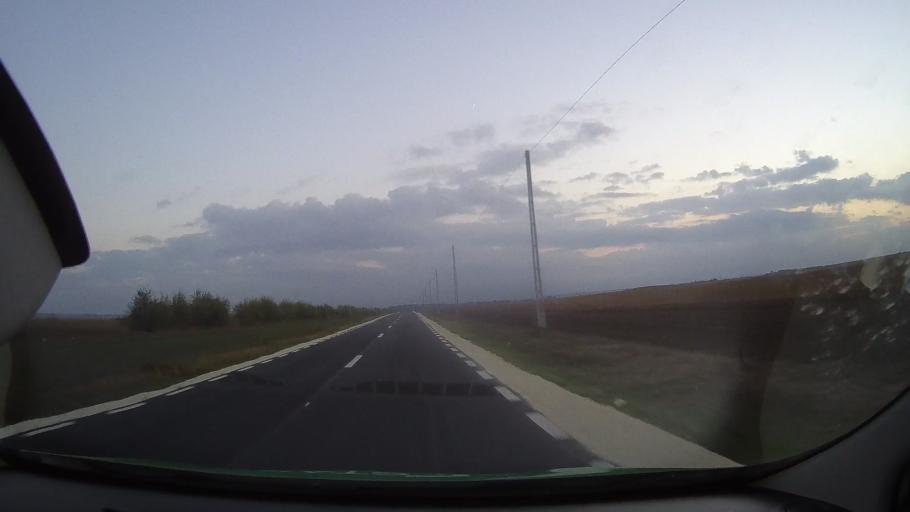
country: RO
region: Constanta
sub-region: Comuna Oltina
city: Oltina
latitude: 44.1270
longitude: 27.6683
